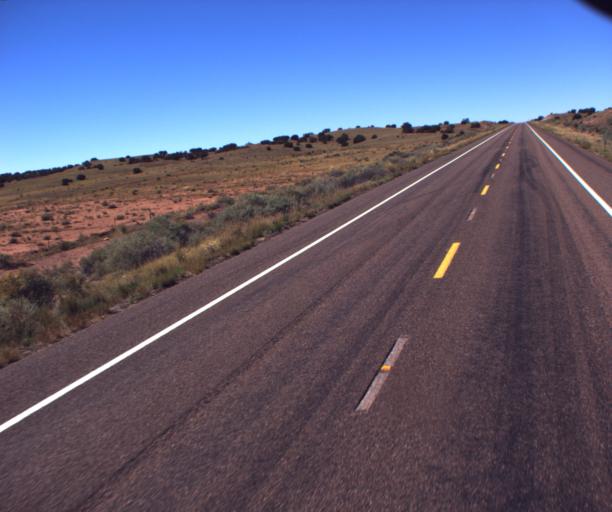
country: US
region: Arizona
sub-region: Apache County
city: Saint Johns
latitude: 34.5933
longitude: -109.6141
